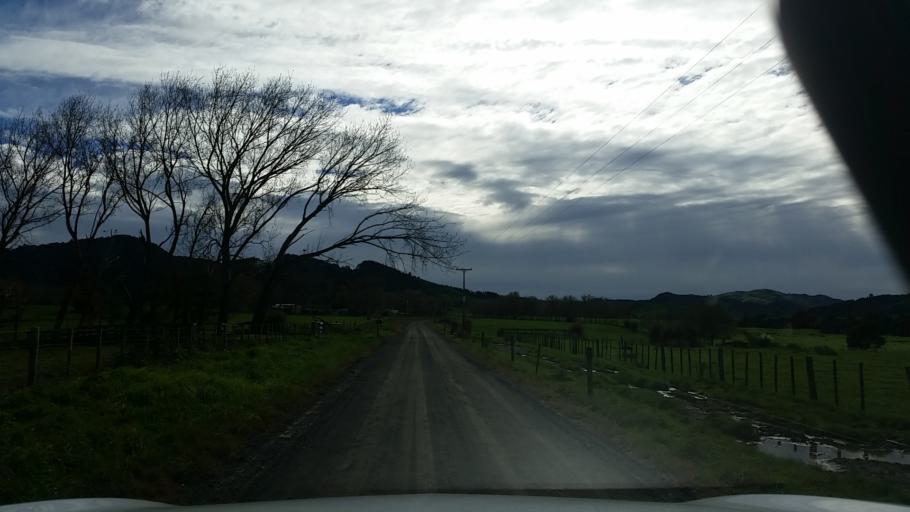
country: NZ
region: Waikato
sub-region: Hauraki District
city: Ngatea
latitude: -37.5076
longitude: 175.4072
